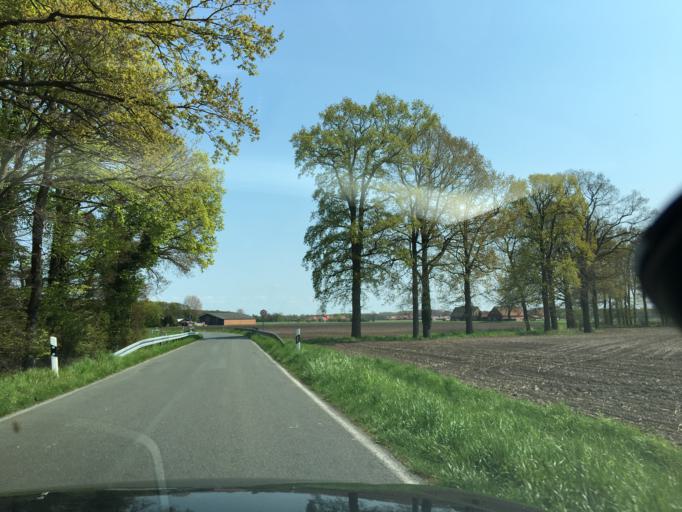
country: DE
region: North Rhine-Westphalia
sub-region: Regierungsbezirk Munster
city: Senden
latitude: 51.8516
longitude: 7.5158
